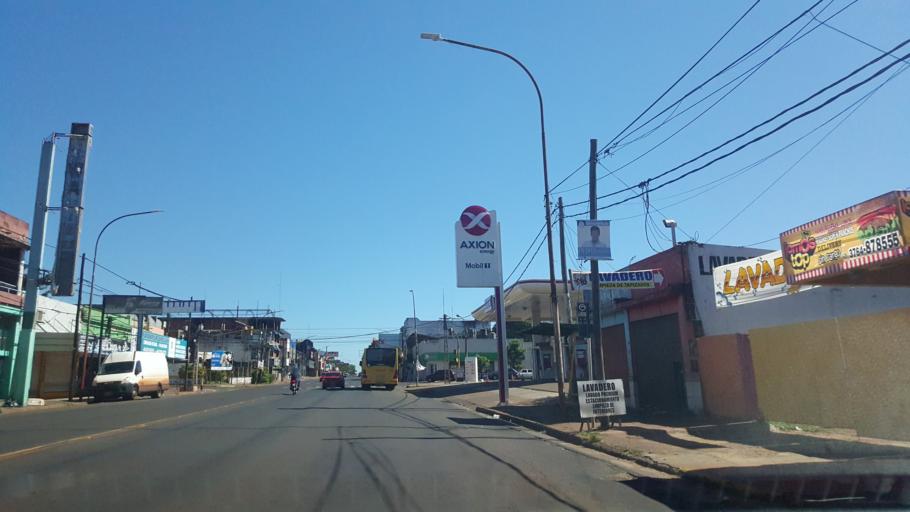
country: AR
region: Misiones
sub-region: Departamento de Capital
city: Posadas
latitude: -27.3835
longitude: -55.8999
